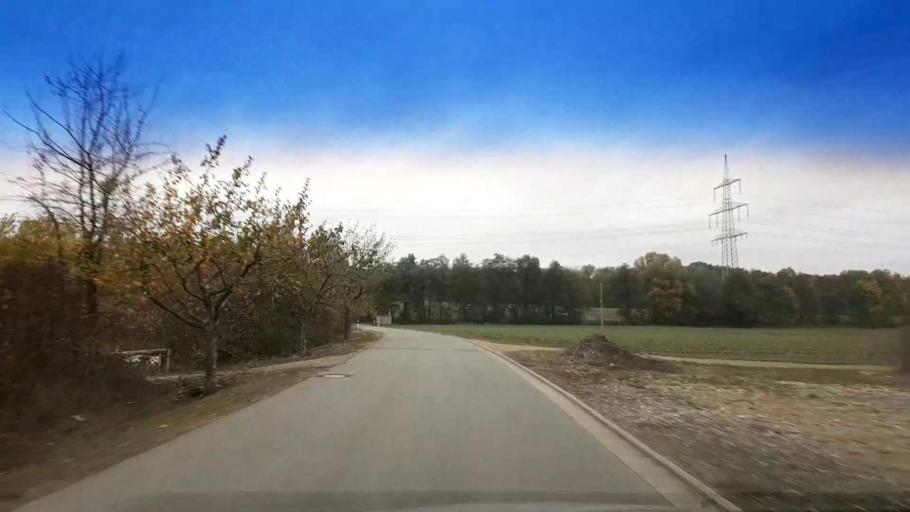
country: DE
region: Bavaria
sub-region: Upper Franconia
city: Schesslitz
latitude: 49.9692
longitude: 11.0312
